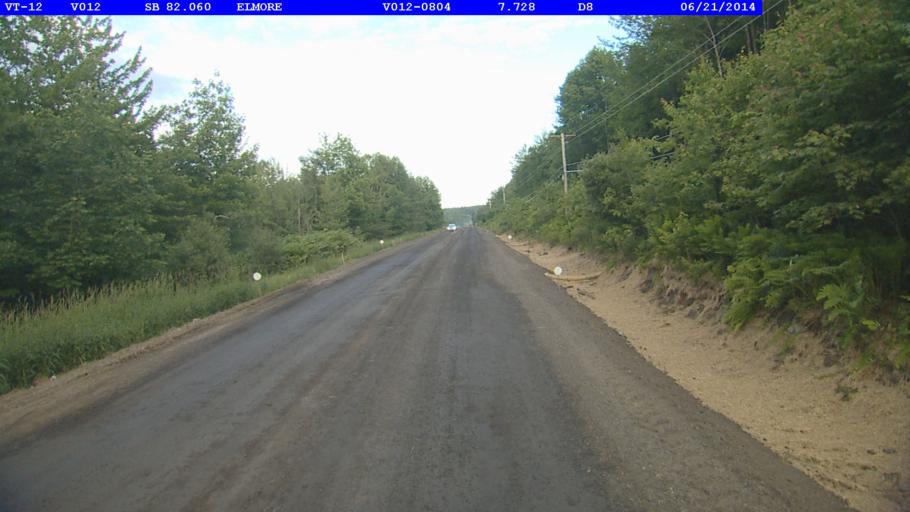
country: US
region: Vermont
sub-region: Lamoille County
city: Morrisville
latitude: 44.5508
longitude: -72.5371
